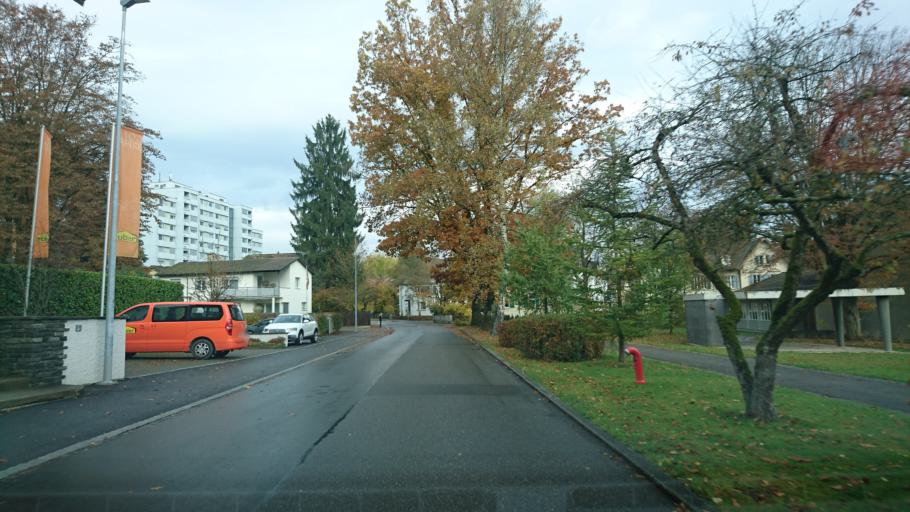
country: CH
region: Aargau
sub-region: Bezirk Aarau
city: Aarau
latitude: 47.3860
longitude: 8.0519
